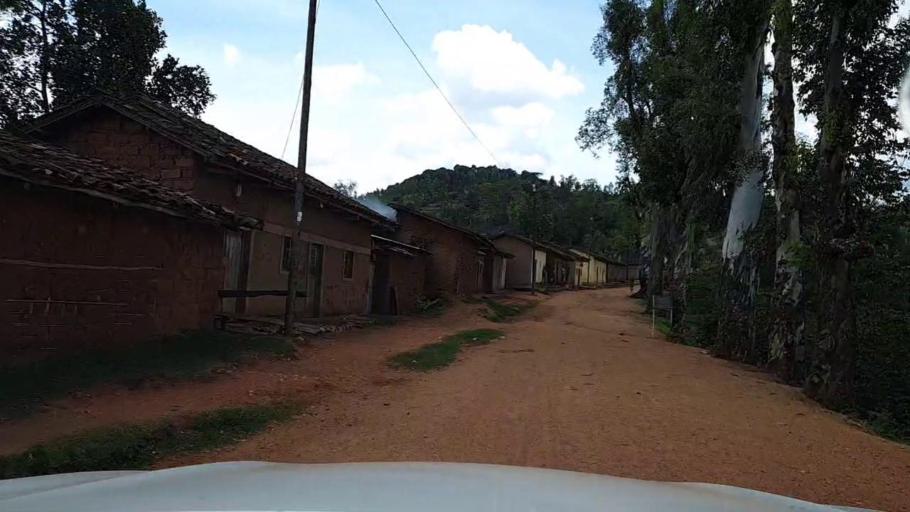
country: RW
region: Southern Province
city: Butare
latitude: -2.7531
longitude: 29.7567
